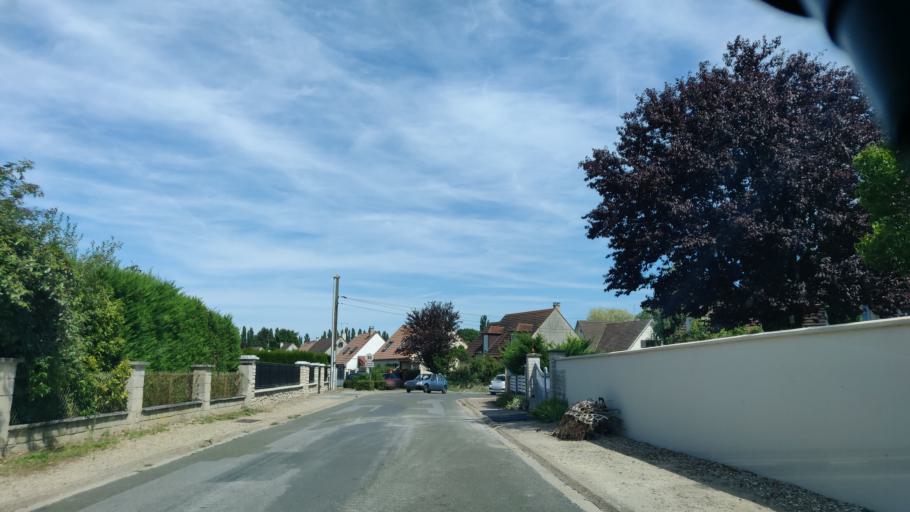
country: FR
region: Picardie
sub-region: Departement de l'Oise
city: Pont-Sainte-Maxence
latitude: 49.3117
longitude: 2.6197
